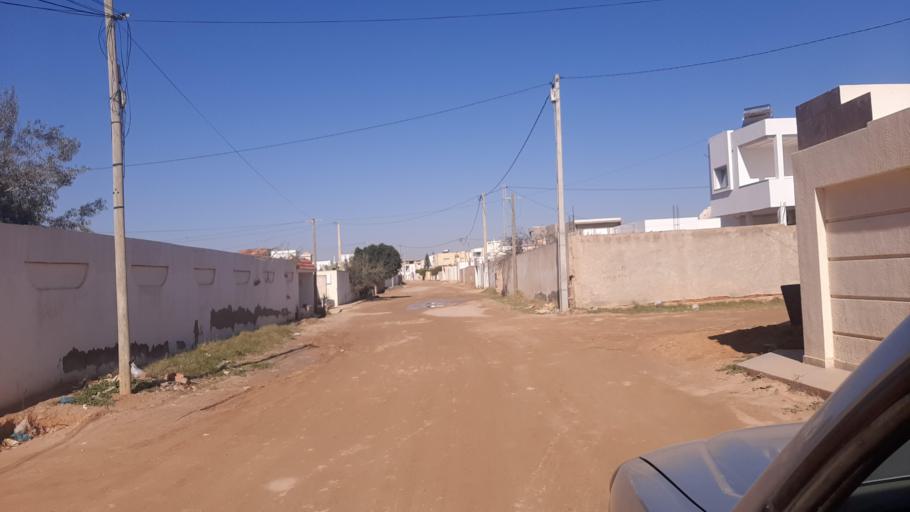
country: TN
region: Safaqis
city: Al Qarmadah
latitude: 34.7906
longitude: 10.8107
